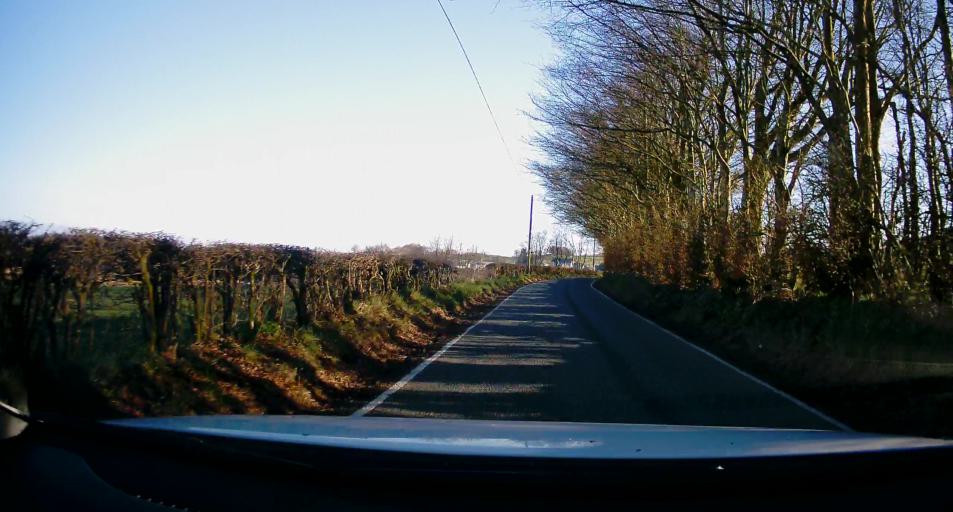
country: GB
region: Wales
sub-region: County of Ceredigion
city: Lledrod
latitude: 52.2668
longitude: -4.0707
